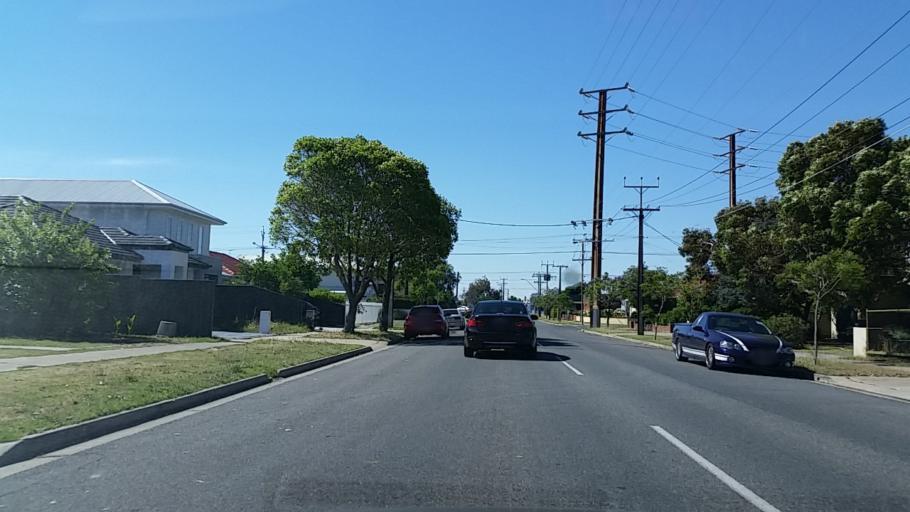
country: AU
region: South Australia
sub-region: Charles Sturt
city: Grange
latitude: -34.9086
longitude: 138.5042
